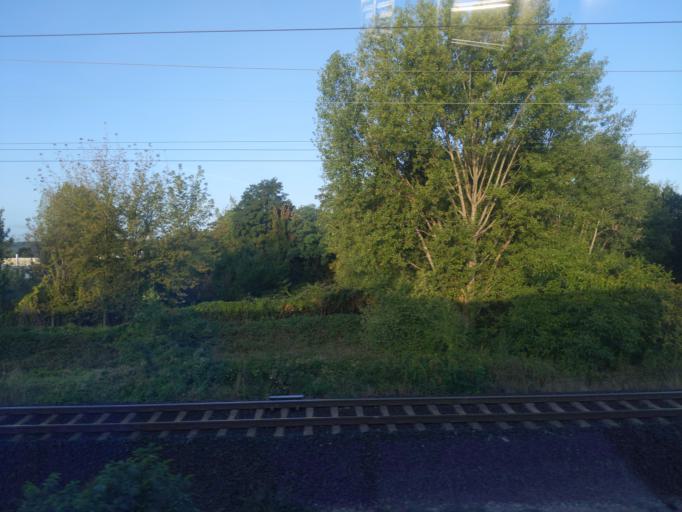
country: DE
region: Saxony
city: Coswig
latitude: 51.1294
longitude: 13.5725
